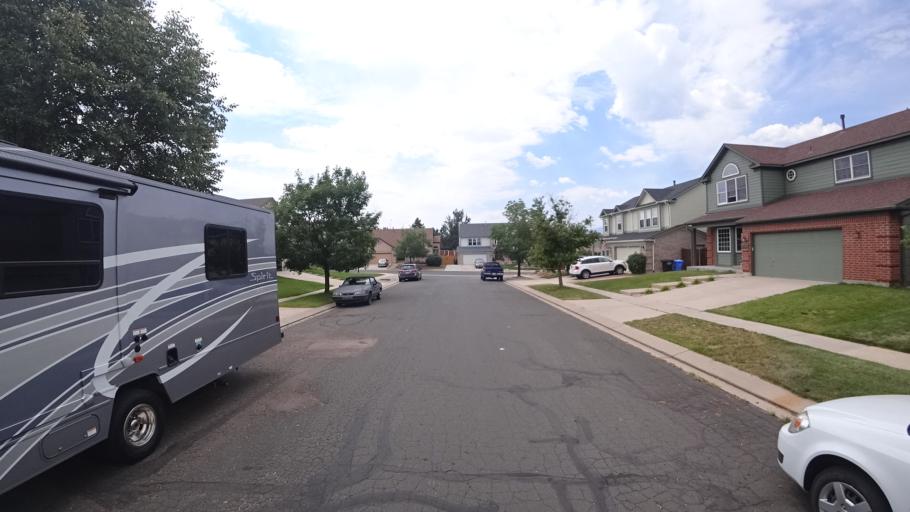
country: US
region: Colorado
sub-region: El Paso County
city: Black Forest
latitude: 38.9599
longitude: -104.7745
